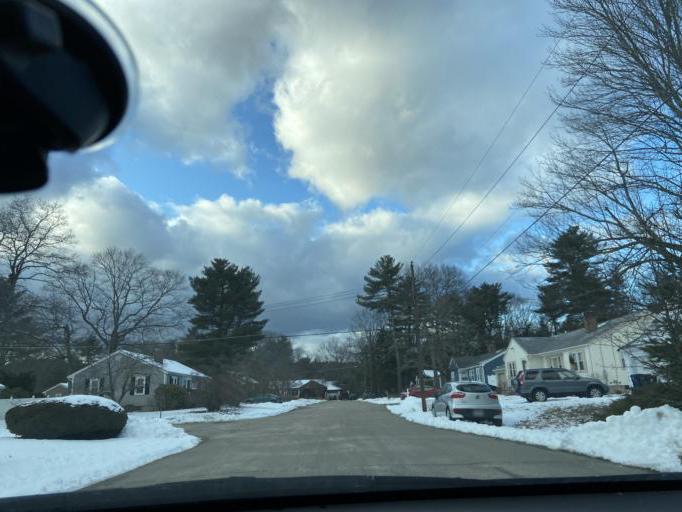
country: US
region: Massachusetts
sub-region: Norfolk County
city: Sharon
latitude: 42.1104
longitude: -71.2015
